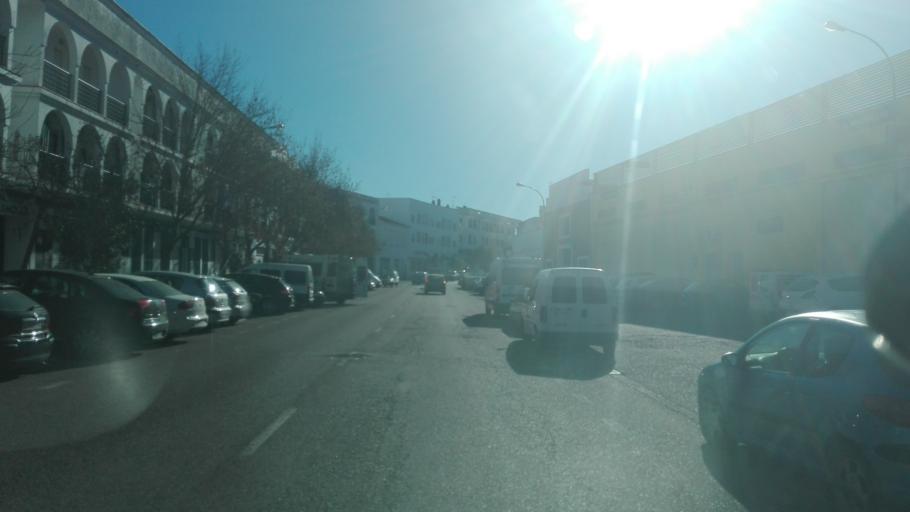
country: ES
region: Extremadura
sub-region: Provincia de Badajoz
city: Llerena
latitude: 38.2400
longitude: -6.0140
